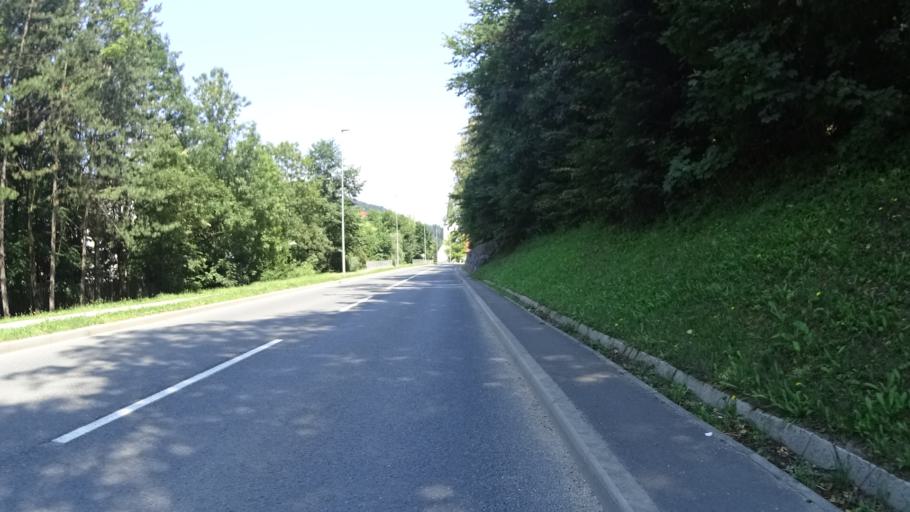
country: SI
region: Ravne na Koroskem
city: Ravne na Koroskem
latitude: 46.5426
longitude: 14.9578
